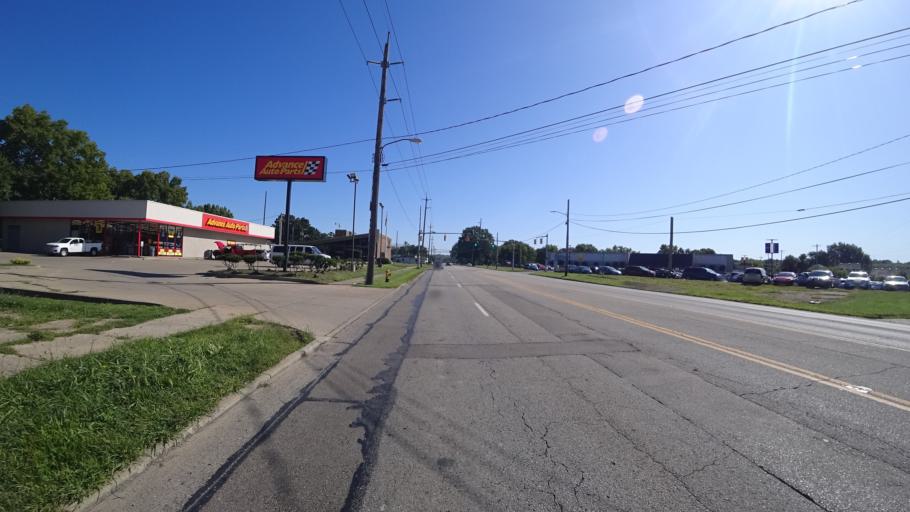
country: US
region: Ohio
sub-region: Butler County
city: Hamilton
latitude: 39.3991
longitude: -84.5461
